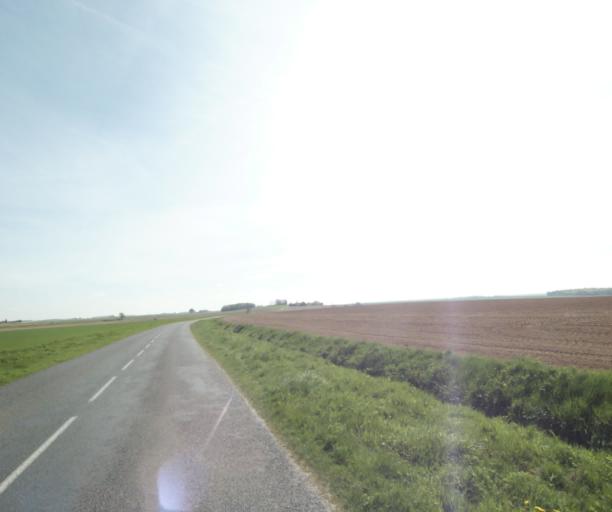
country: FR
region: Ile-de-France
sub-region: Departement de Seine-et-Marne
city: Nangis
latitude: 48.5553
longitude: 3.0289
